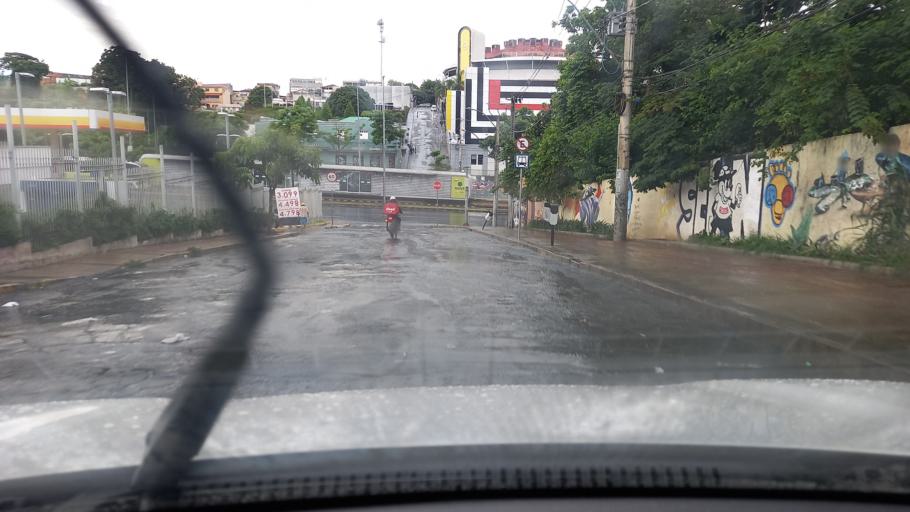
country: BR
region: Minas Gerais
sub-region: Belo Horizonte
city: Belo Horizonte
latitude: -19.9007
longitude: -43.9468
